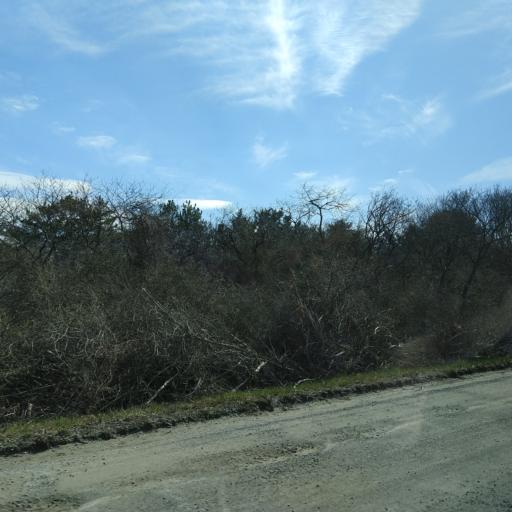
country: US
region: Massachusetts
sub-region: Essex County
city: Ipswich
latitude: 42.7100
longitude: -70.7756
